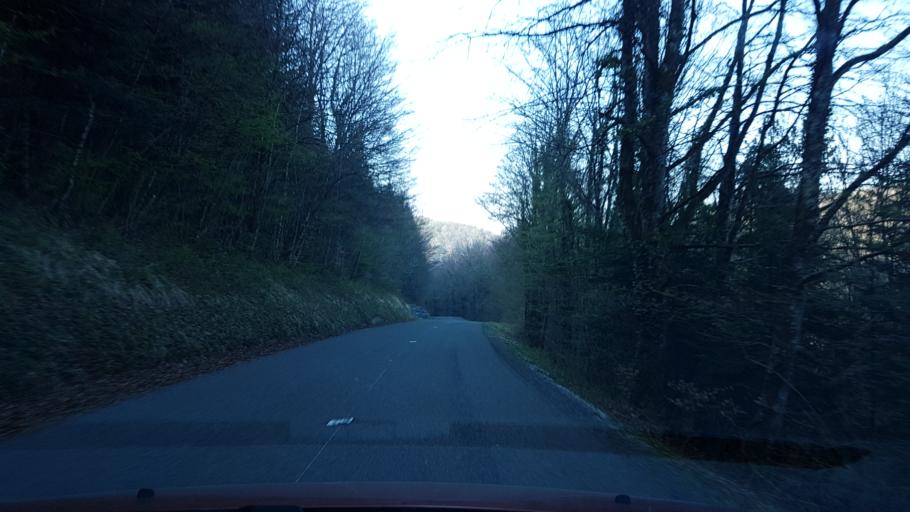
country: FR
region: Bourgogne
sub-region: Departement de Saone-et-Loire
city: Cuiseaux
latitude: 46.4861
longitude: 5.4820
